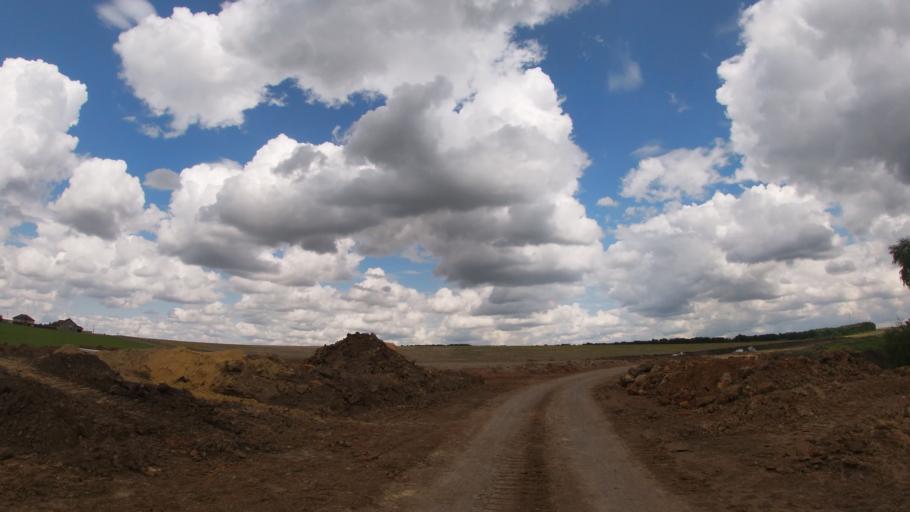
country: RU
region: Belgorod
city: Mayskiy
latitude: 50.5177
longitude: 36.4921
